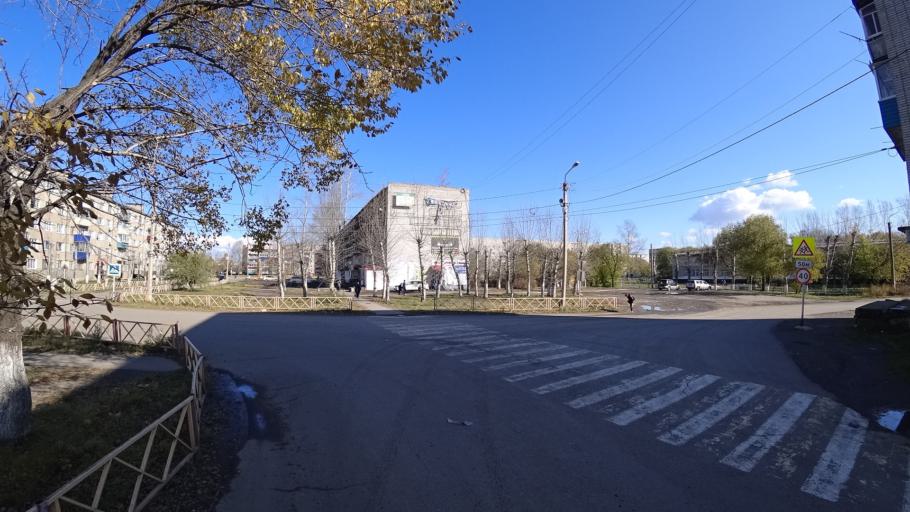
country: RU
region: Khabarovsk Krai
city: Amursk
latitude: 50.0986
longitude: 136.5125
